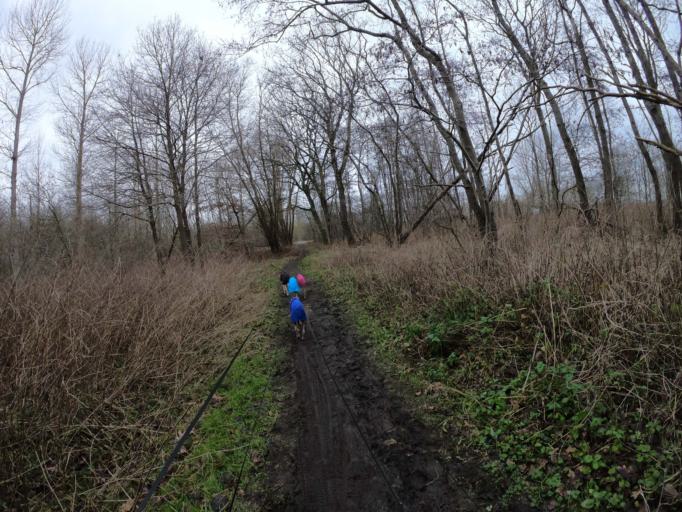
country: BE
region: Flanders
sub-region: Provincie Vlaams-Brabant
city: Tremelo
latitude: 50.9695
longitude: 4.6808
